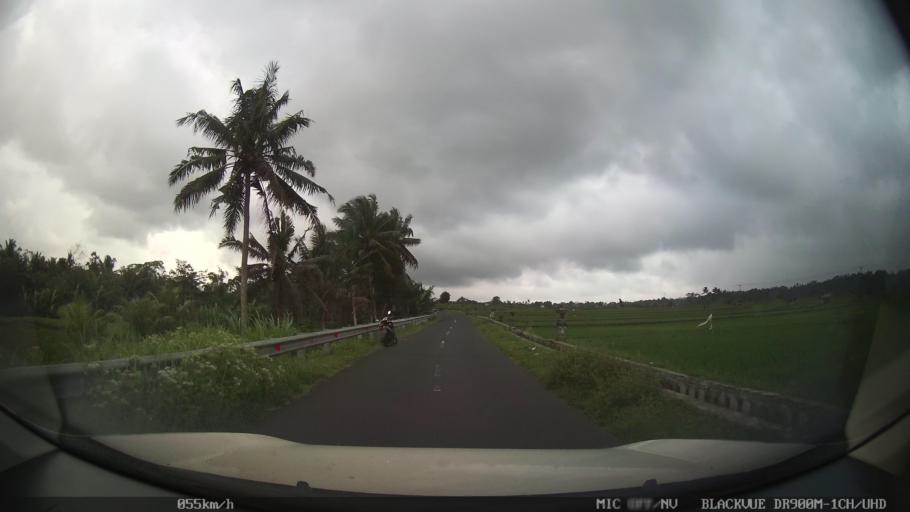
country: ID
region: Bali
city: Banjar Sempidi
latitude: -8.5199
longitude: 115.1955
